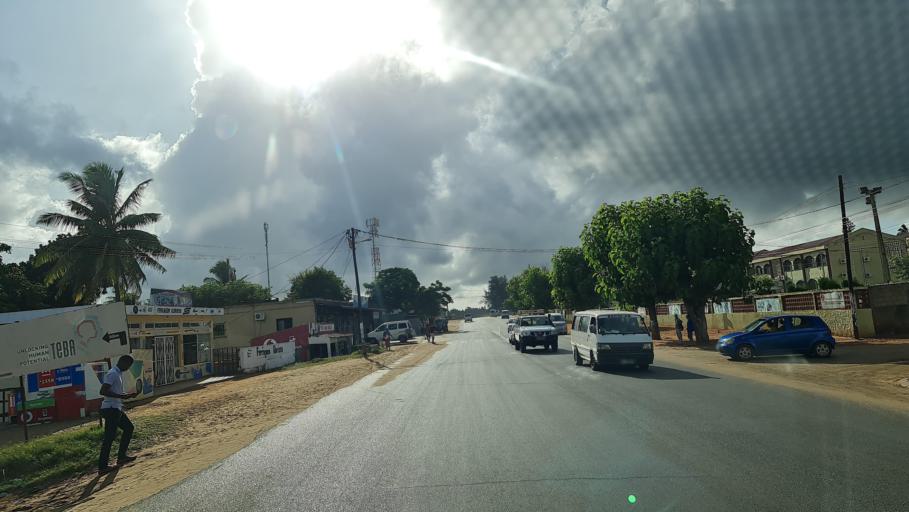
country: MZ
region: Gaza
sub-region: Xai-Xai District
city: Xai-Xai
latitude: -25.0555
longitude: 33.6689
